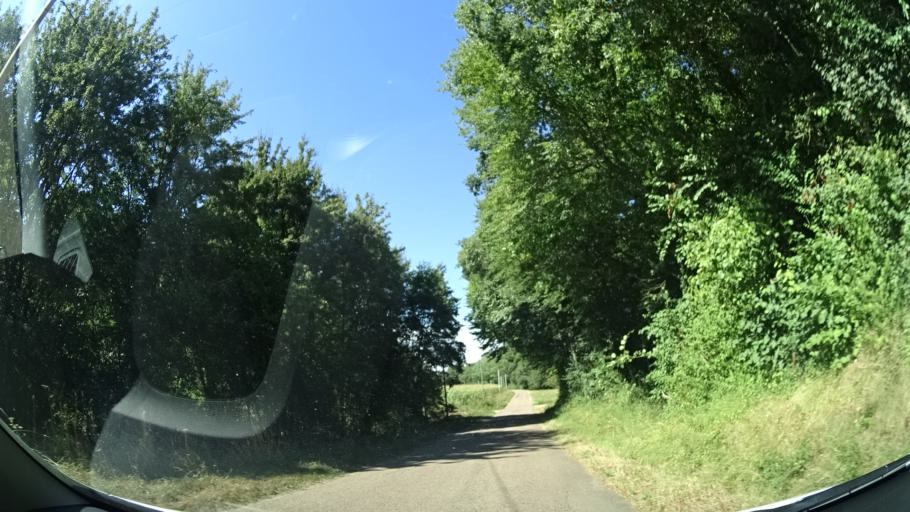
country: FR
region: Centre
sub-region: Departement du Loiret
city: Trigueres
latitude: 47.9478
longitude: 2.9848
